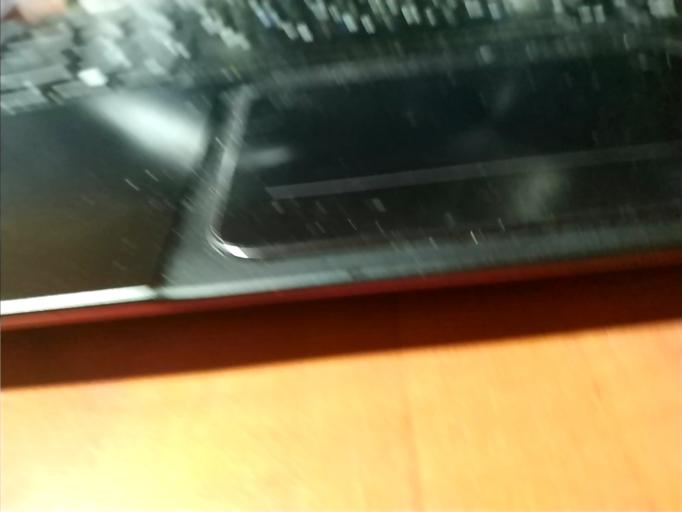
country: RU
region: Tverskaya
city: Ves'yegonsk
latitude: 58.6990
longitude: 37.5439
